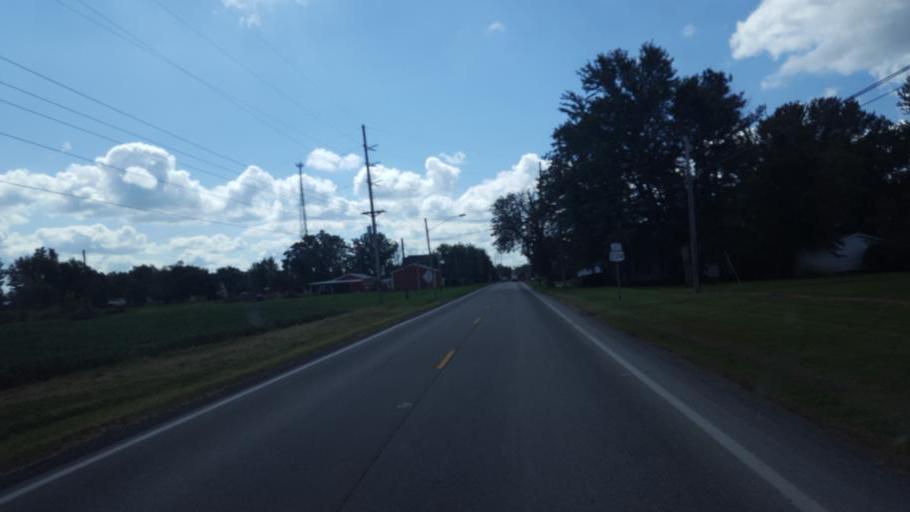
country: US
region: Ohio
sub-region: Wayne County
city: West Salem
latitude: 41.0297
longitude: -82.1262
